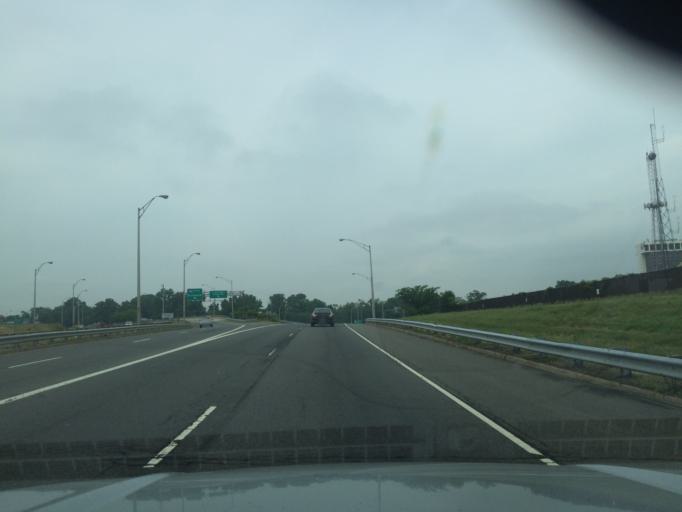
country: US
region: Virginia
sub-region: Arlington County
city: Arlington
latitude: 38.8666
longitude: -77.0664
